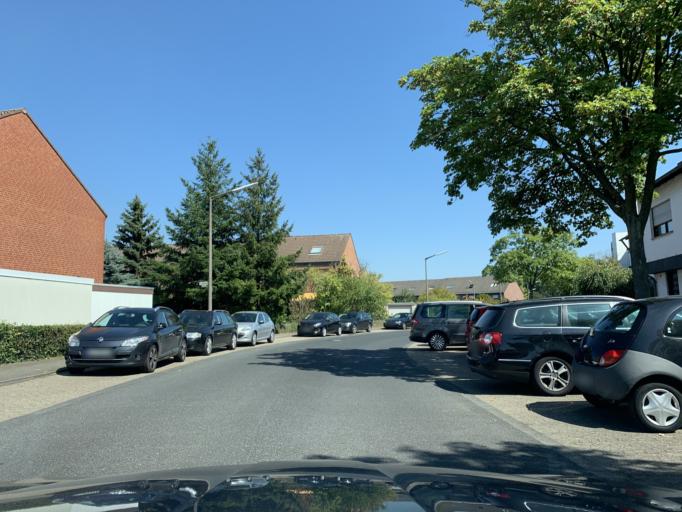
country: DE
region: North Rhine-Westphalia
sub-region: Regierungsbezirk Koln
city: Mengenich
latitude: 50.9996
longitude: 6.8682
